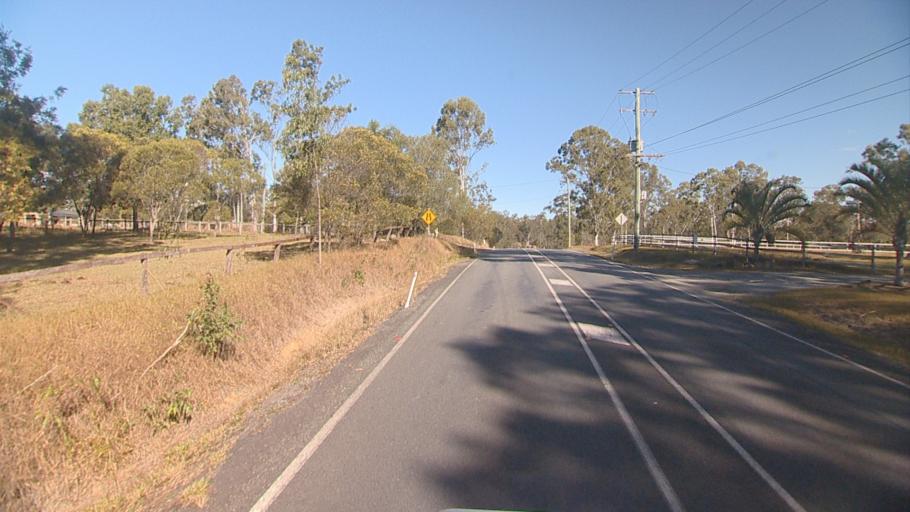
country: AU
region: Queensland
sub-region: Logan
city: Cedar Vale
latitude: -27.8306
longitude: 153.0530
